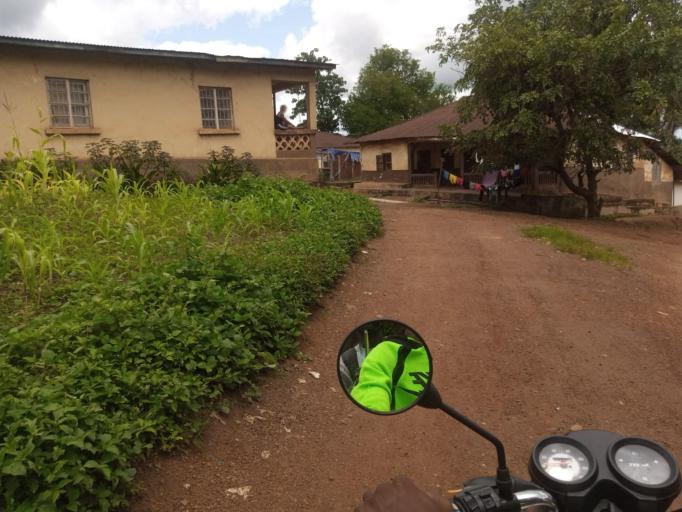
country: SL
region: Northern Province
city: Port Loko
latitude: 8.7641
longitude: -12.7844
